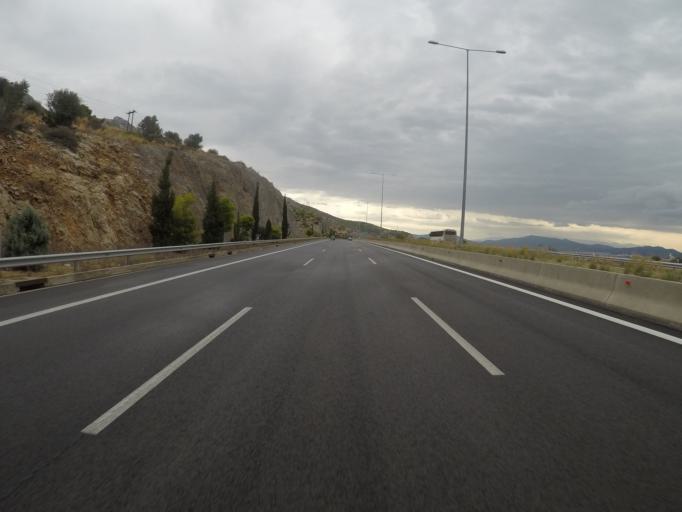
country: GR
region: Attica
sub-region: Nomarchia Dytikis Attikis
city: Vlychada
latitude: 38.0279
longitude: 23.4546
